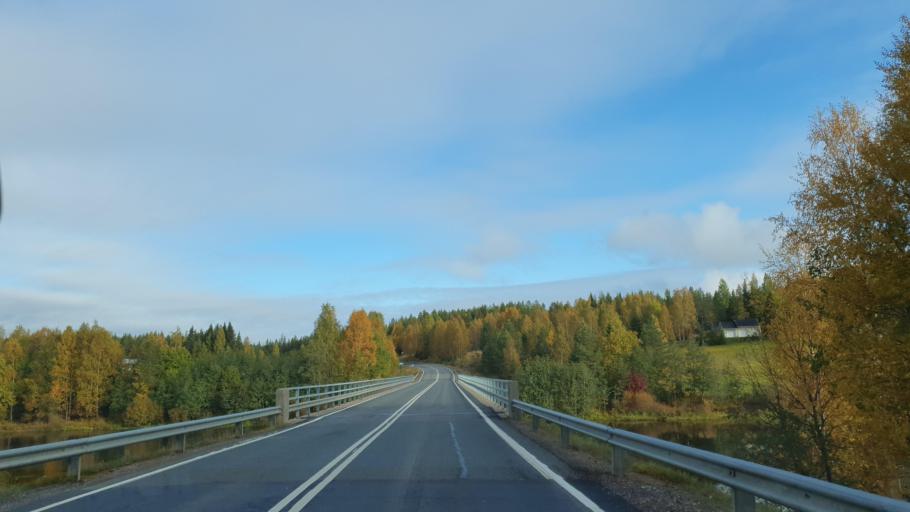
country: FI
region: Kainuu
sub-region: Kehys-Kainuu
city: Puolanka
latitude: 65.3284
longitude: 27.4445
